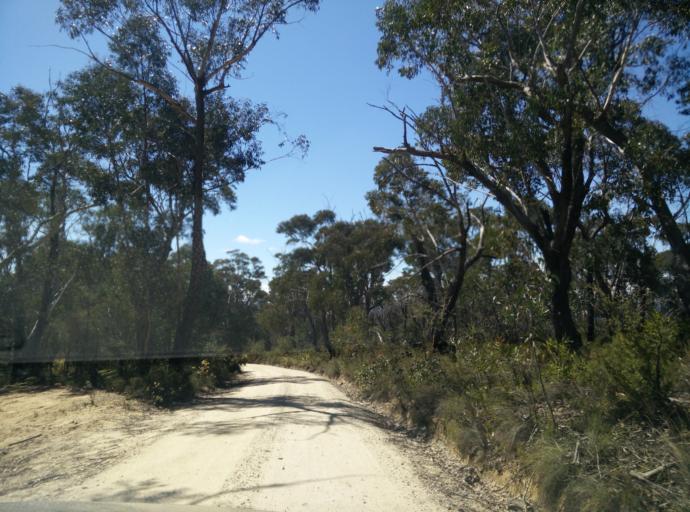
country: AU
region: New South Wales
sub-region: Blue Mountains Municipality
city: Blackheath
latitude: -33.5692
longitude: 150.2795
